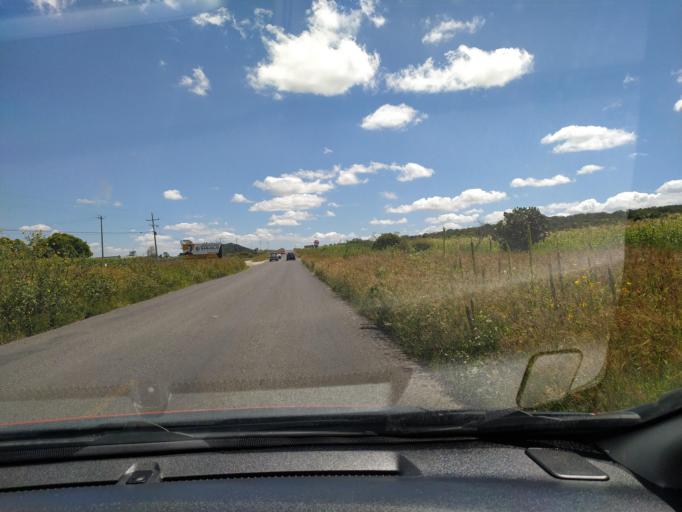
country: MX
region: Jalisco
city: San Julian
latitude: 21.0070
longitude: -102.1318
